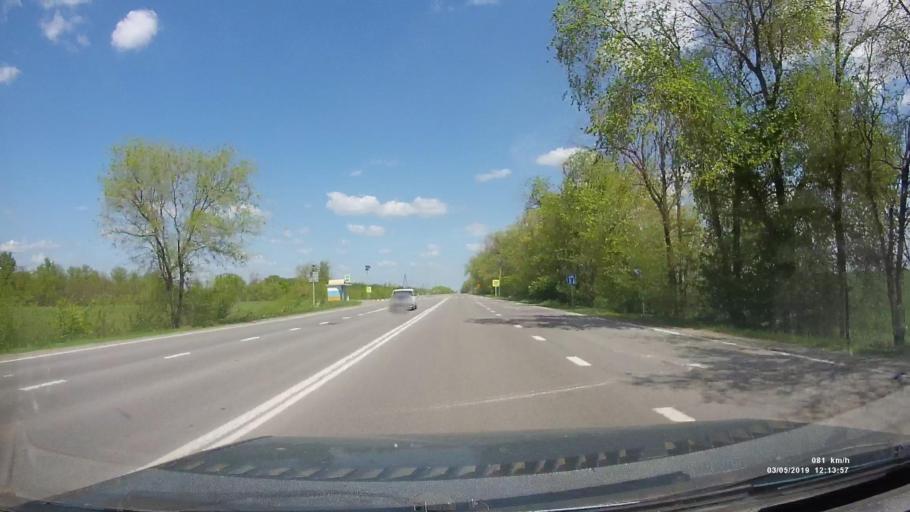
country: RU
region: Rostov
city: Melikhovskaya
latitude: 47.3376
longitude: 40.5586
